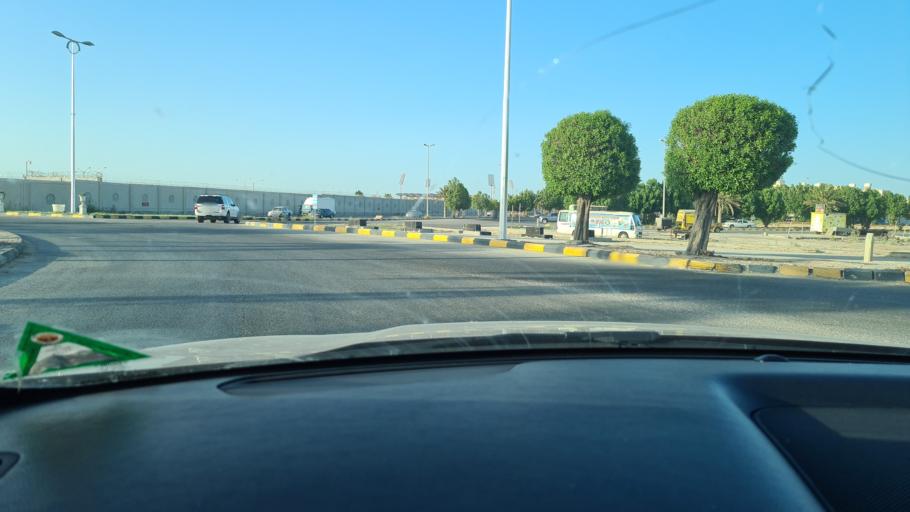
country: SA
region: Eastern Province
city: Al Jubayl
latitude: 26.9269
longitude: 49.7120
